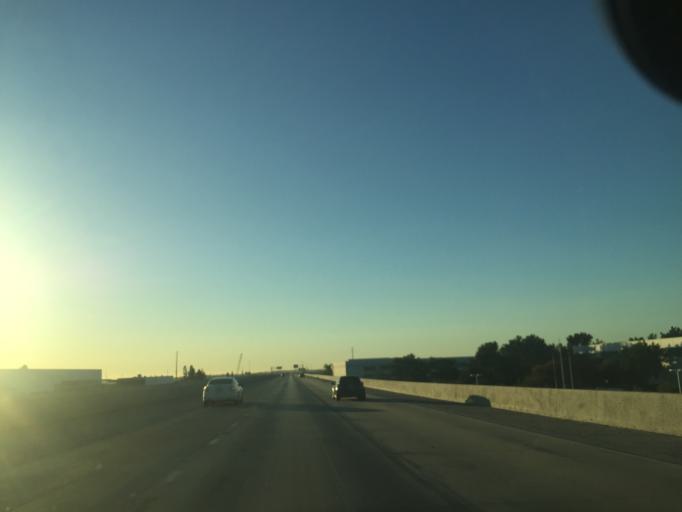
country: MX
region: Baja California
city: Tijuana
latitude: 32.5640
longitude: -116.9366
